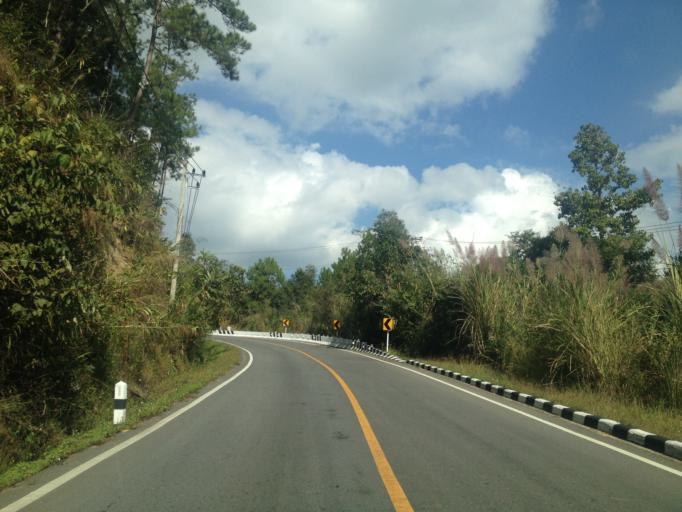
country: TH
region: Mae Hong Son
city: Ban Huai I Huak
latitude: 18.1487
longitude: 98.1610
